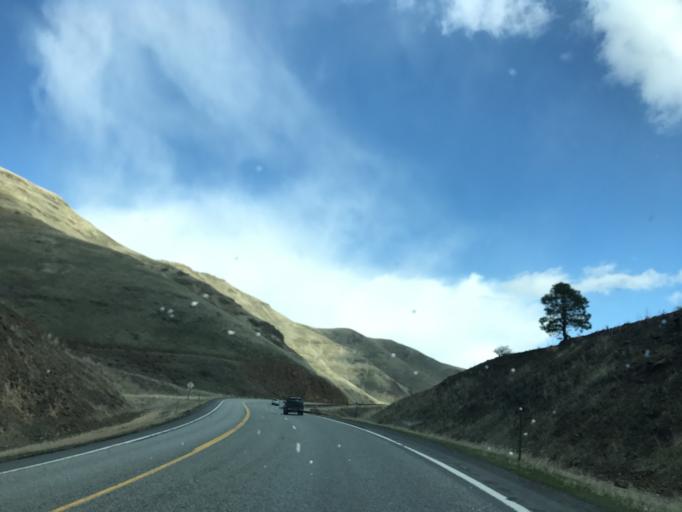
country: US
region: Idaho
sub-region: Idaho County
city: Grangeville
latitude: 45.7894
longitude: -116.2914
